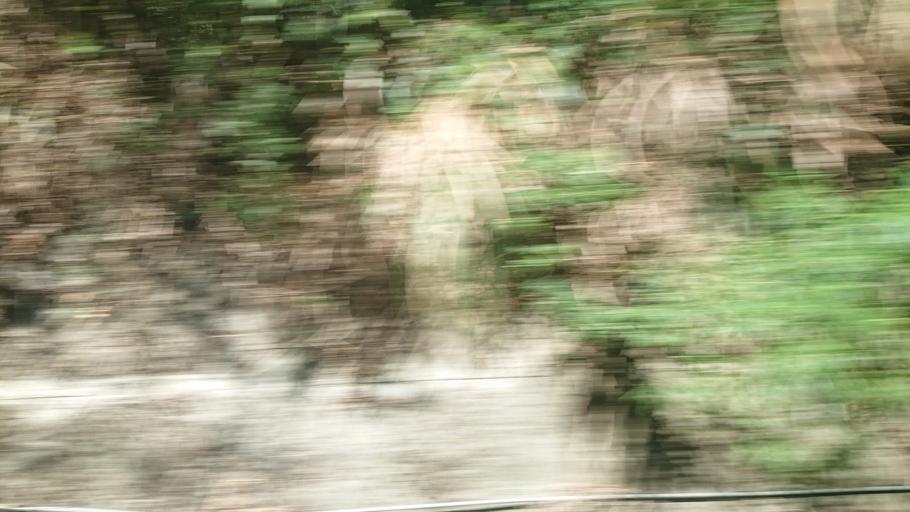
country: TW
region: Taiwan
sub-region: Chiayi
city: Jiayi Shi
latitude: 23.5316
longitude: 120.6447
